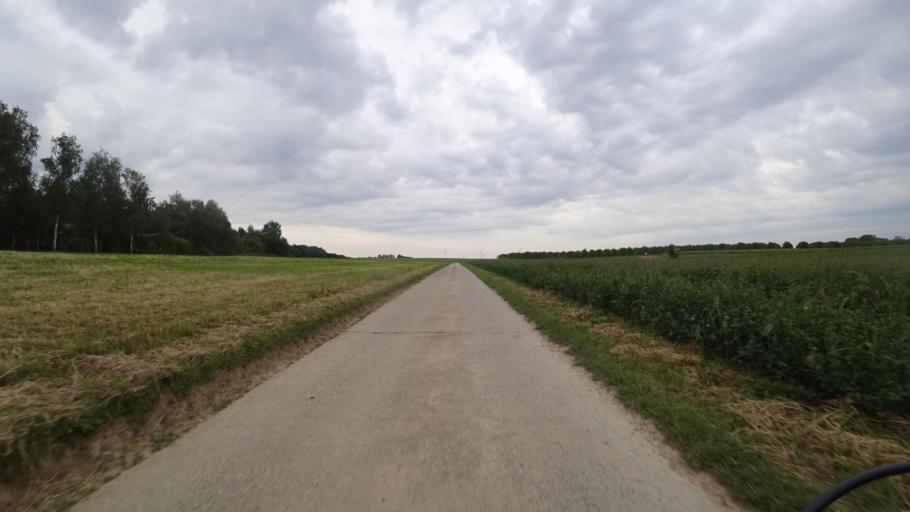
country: BE
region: Wallonia
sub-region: Province de Namur
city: Gembloux
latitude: 50.5827
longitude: 4.7460
